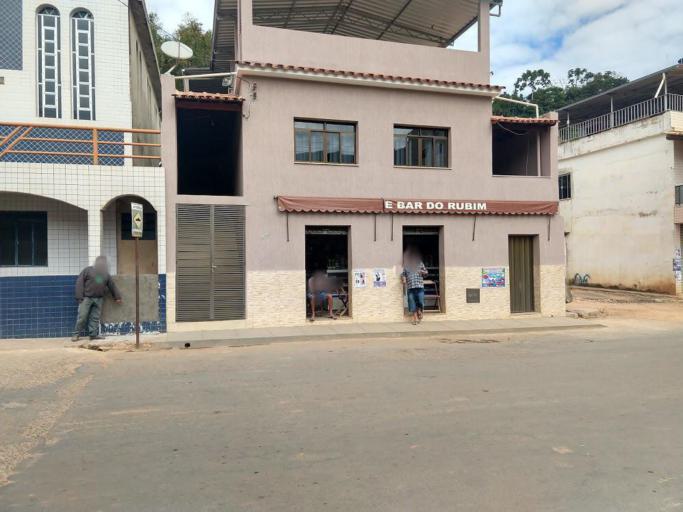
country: BR
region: Minas Gerais
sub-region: Vicosa
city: Vicosa
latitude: -20.6848
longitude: -42.6225
